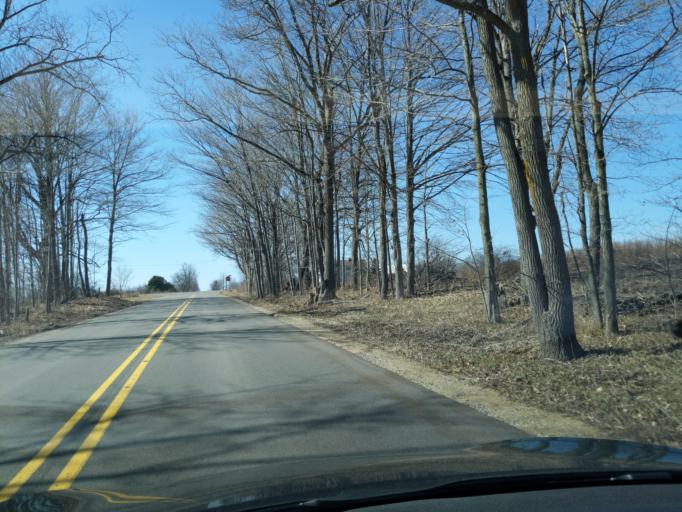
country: US
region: Michigan
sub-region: Ionia County
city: Lake Odessa
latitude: 42.7267
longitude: -84.9936
